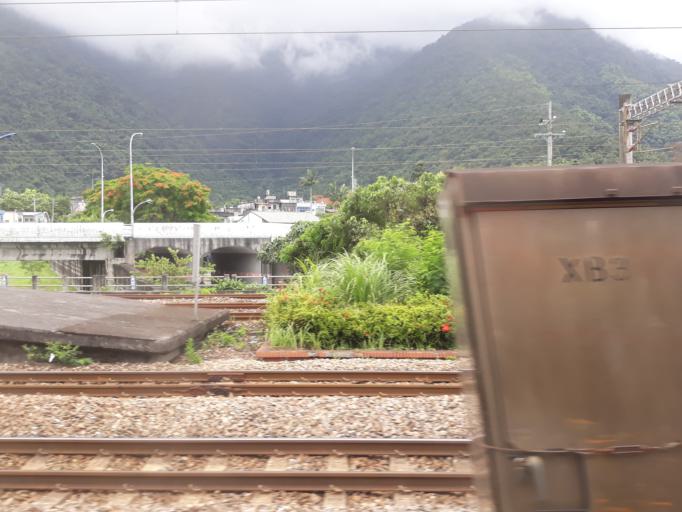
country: TW
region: Taiwan
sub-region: Yilan
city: Yilan
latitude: 24.4628
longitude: 121.8025
